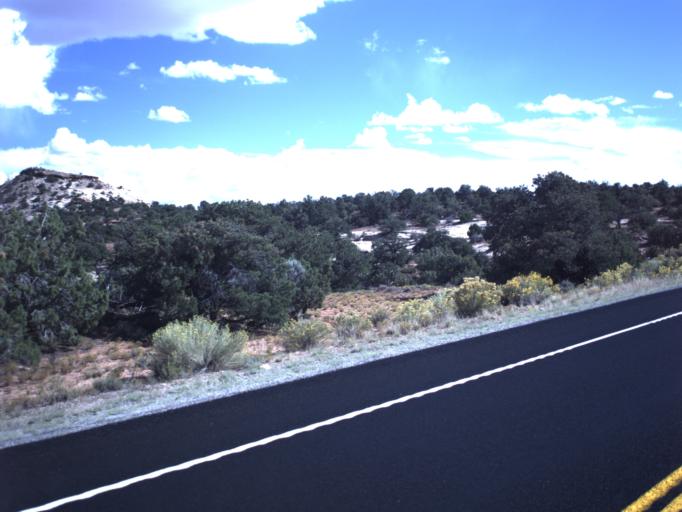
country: US
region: Utah
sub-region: Grand County
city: Moab
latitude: 38.5569
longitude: -109.7926
